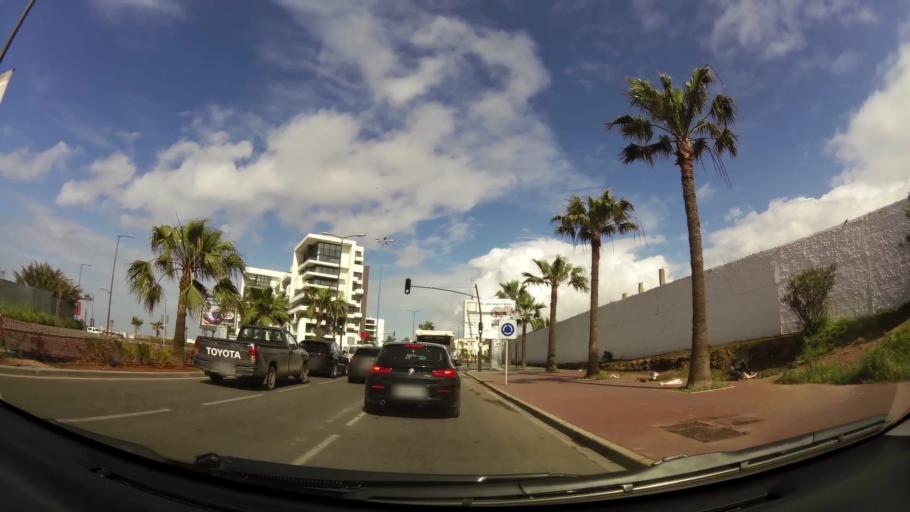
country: MA
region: Grand Casablanca
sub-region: Casablanca
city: Casablanca
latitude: 33.5706
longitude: -7.7009
